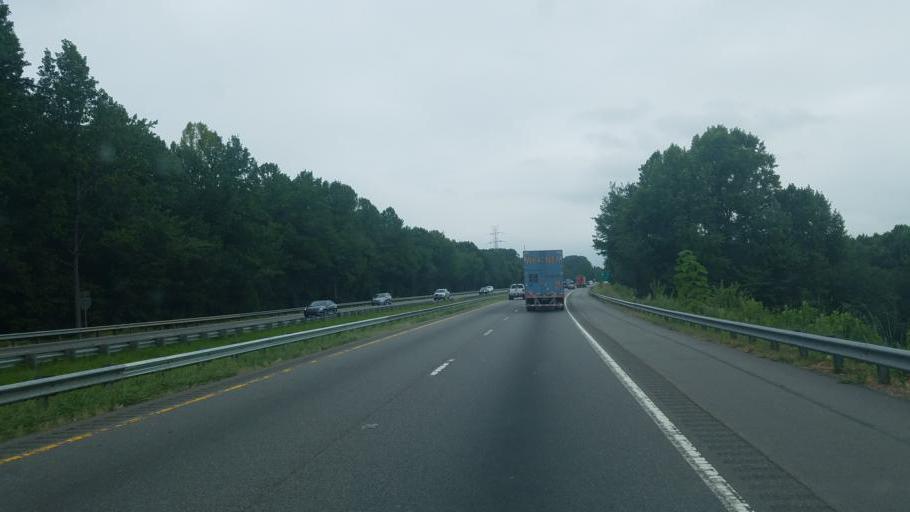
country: US
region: North Carolina
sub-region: Iredell County
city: Troutman
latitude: 35.6665
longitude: -80.8598
